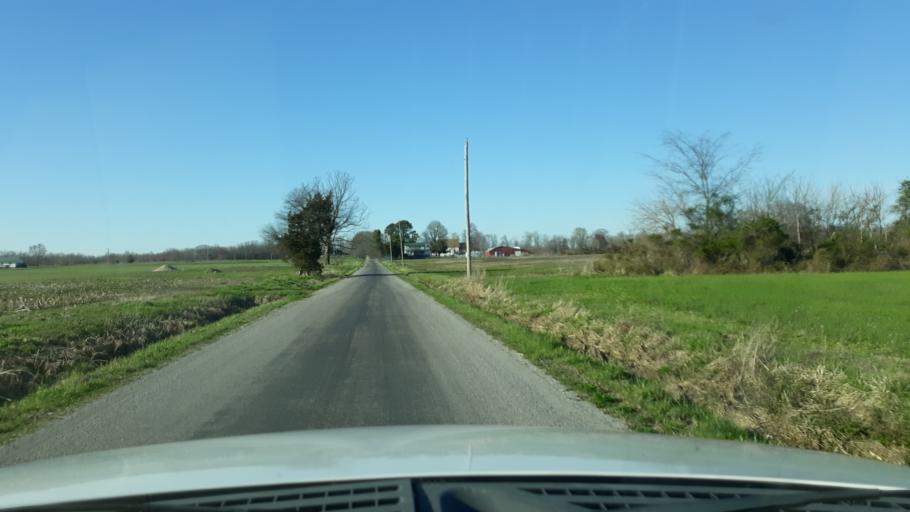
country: US
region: Illinois
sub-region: Saline County
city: Harrisburg
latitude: 37.8008
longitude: -88.6055
